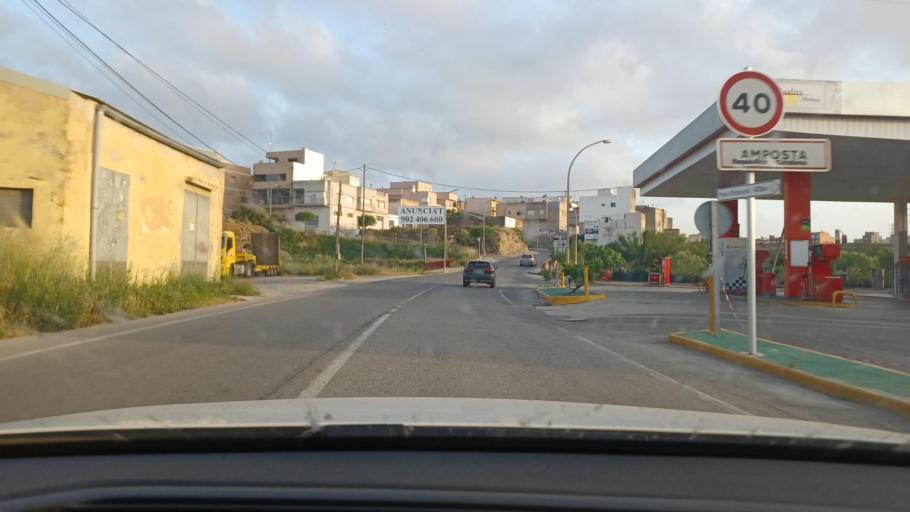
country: ES
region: Catalonia
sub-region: Provincia de Tarragona
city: Amposta
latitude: 40.7171
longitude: 0.5751
